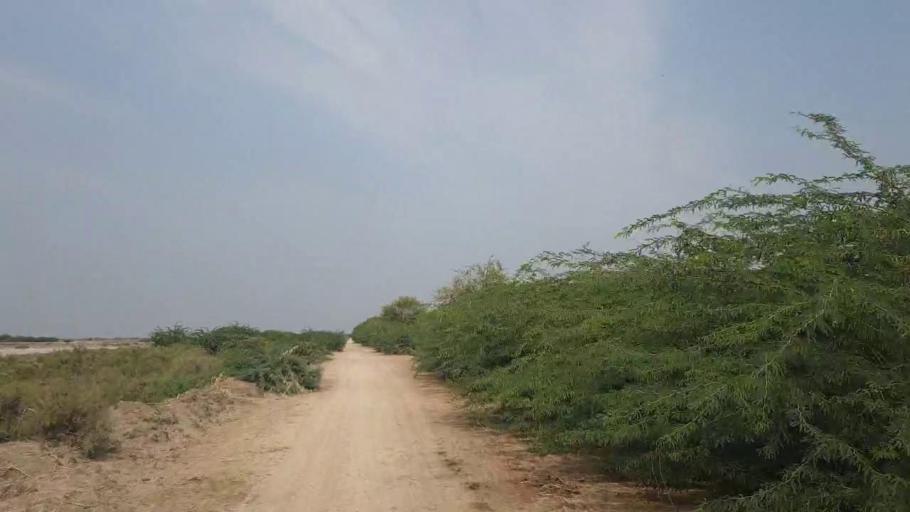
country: PK
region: Sindh
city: Badin
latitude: 24.5586
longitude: 68.7323
